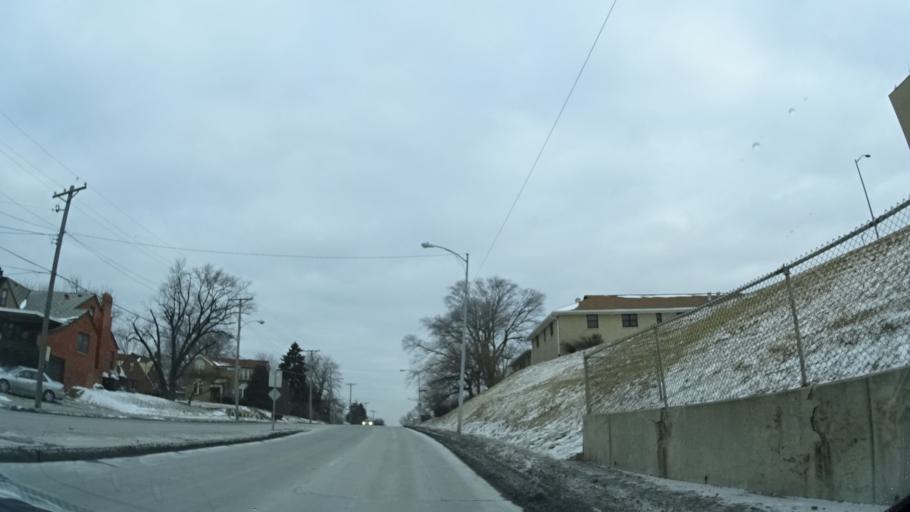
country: US
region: Nebraska
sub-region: Douglas County
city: Omaha
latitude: 41.2423
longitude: -95.9757
